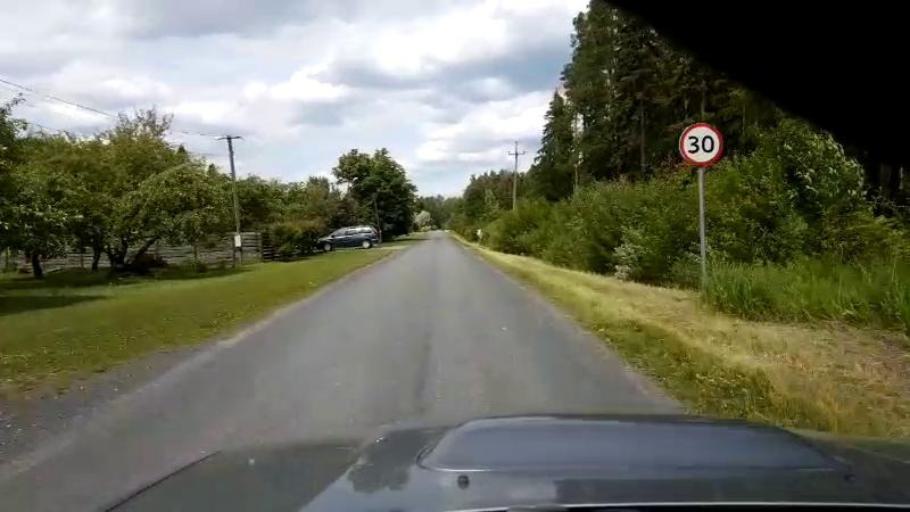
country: EE
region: Paernumaa
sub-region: Halinga vald
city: Parnu-Jaagupi
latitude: 58.5228
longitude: 24.5635
